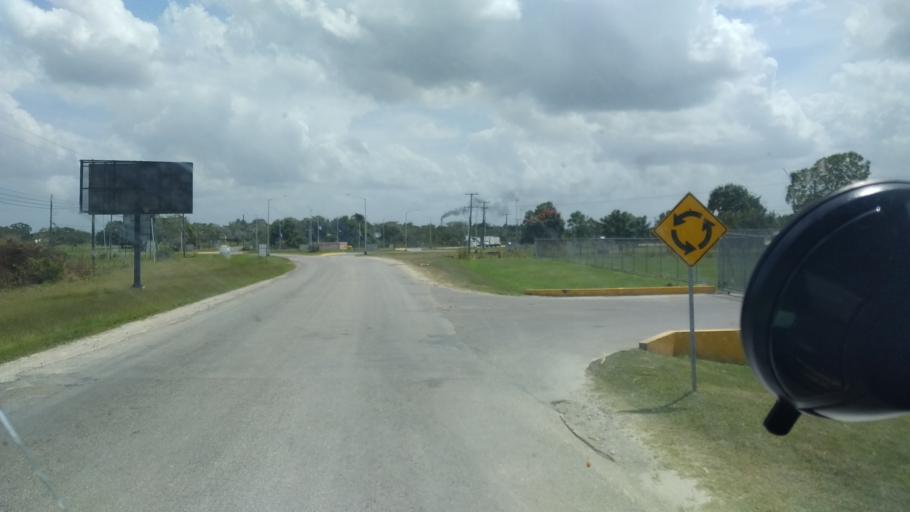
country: BZ
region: Orange Walk
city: Orange Walk
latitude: 18.0564
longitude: -88.5666
